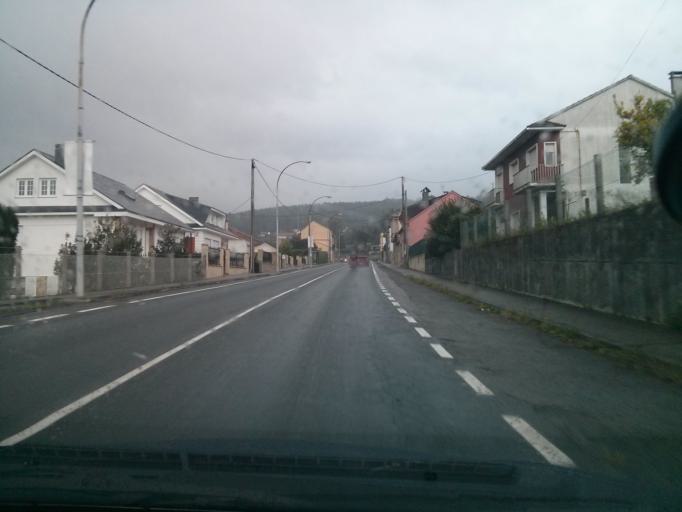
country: ES
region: Galicia
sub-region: Provincia da Coruna
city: Noia
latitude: 42.7998
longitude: -8.8856
